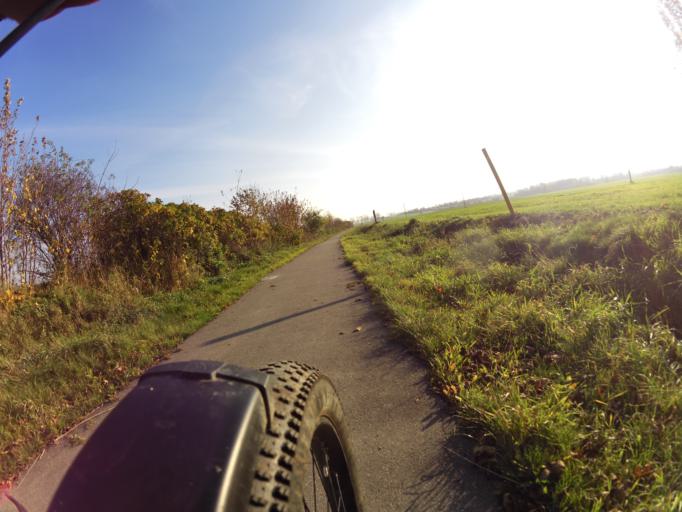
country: PL
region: Pomeranian Voivodeship
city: Strzelno
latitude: 54.7652
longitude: 18.2499
